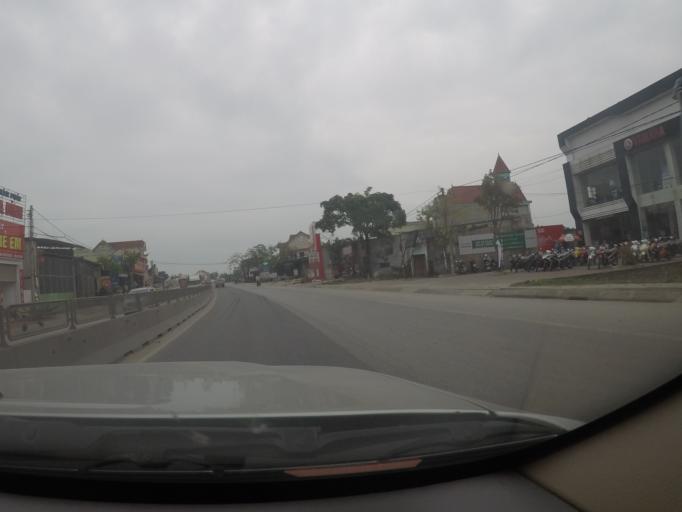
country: VN
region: Nghe An
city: Dien Chau
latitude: 19.0055
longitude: 105.5898
